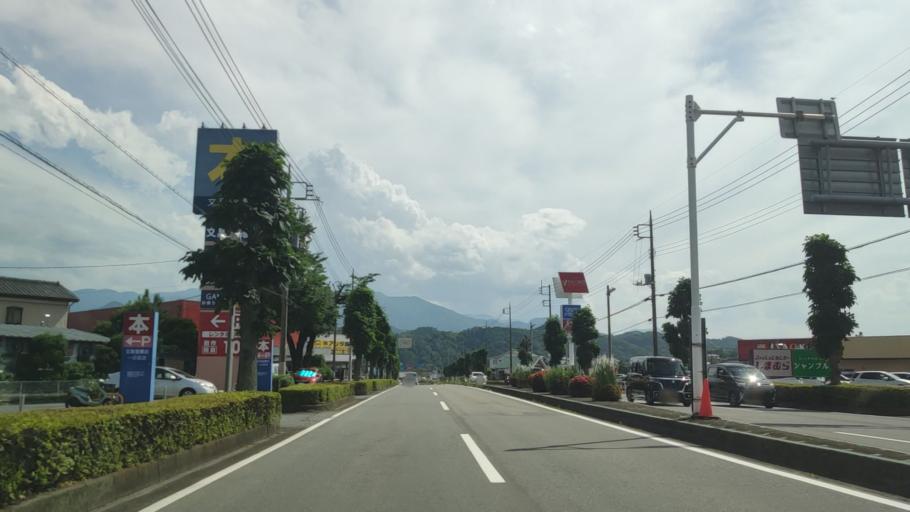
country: JP
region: Gunma
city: Tomioka
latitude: 36.2503
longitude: 138.8607
